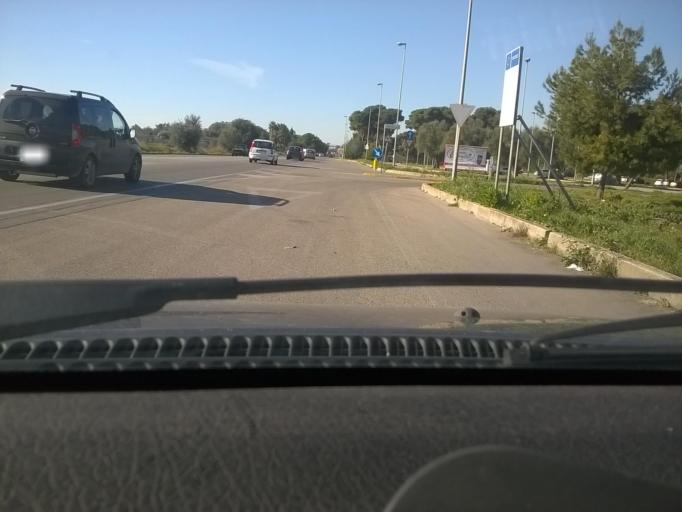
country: IT
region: Apulia
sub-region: Provincia di Taranto
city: Paolo VI
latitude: 40.4658
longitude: 17.3008
